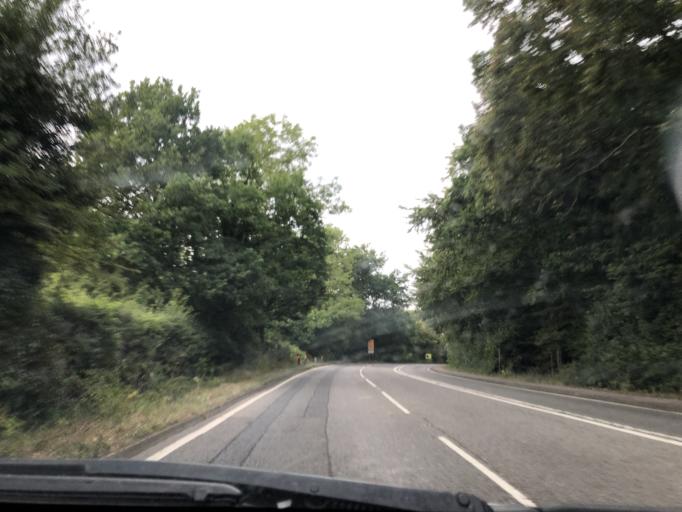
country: GB
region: England
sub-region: Kent
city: Sevenoaks
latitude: 51.2455
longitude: 0.2067
